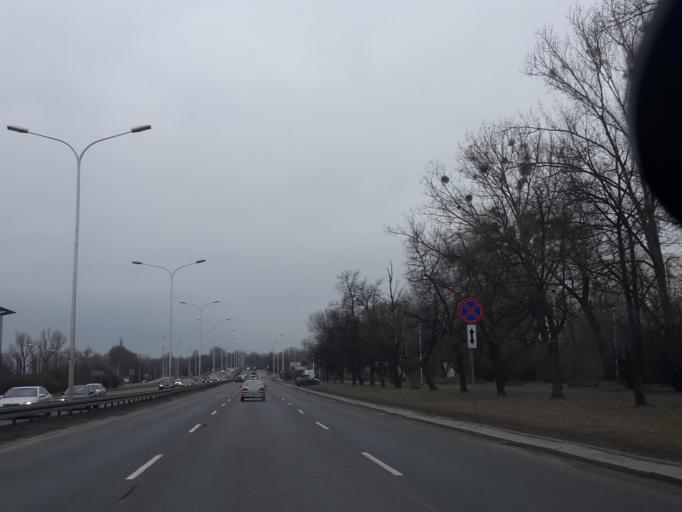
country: PL
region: Masovian Voivodeship
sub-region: Warszawa
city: Zoliborz
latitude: 52.2767
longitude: 20.9941
